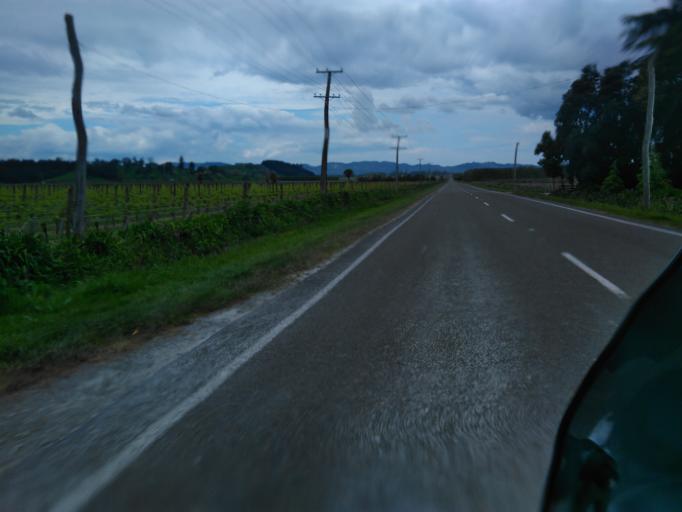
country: NZ
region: Gisborne
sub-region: Gisborne District
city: Gisborne
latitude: -38.6445
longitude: 177.8661
